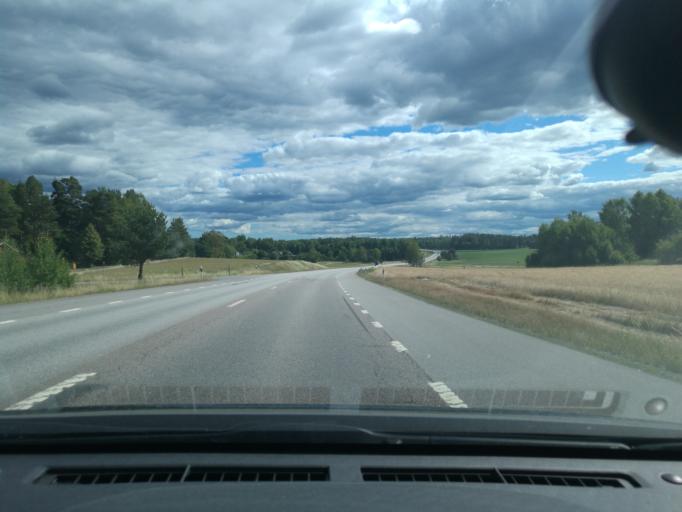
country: SE
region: OEstergoetland
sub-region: Soderkopings Kommun
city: Soederkoeping
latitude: 58.4576
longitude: 16.3655
